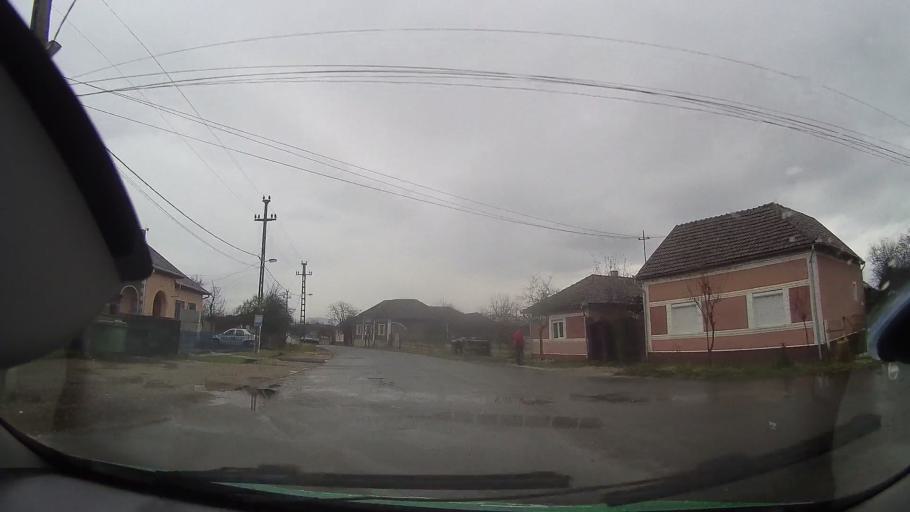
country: RO
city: Capalna
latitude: 46.7370
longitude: 22.1019
